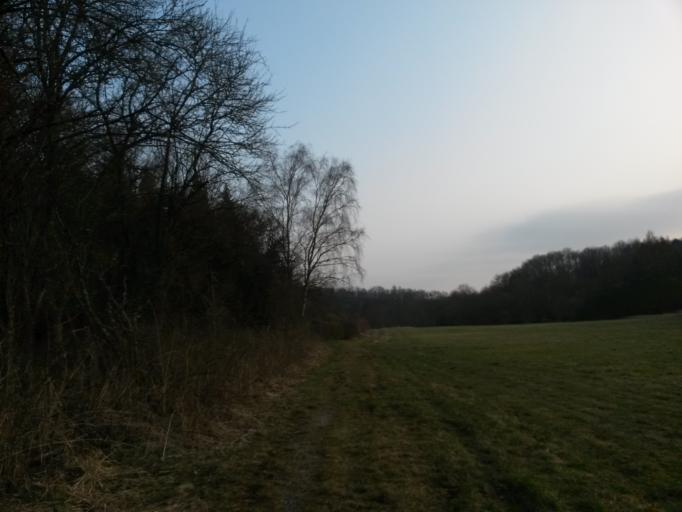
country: DE
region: Bavaria
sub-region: Regierungsbezirk Unterfranken
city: Rimpar
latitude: 49.8402
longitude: 9.9598
